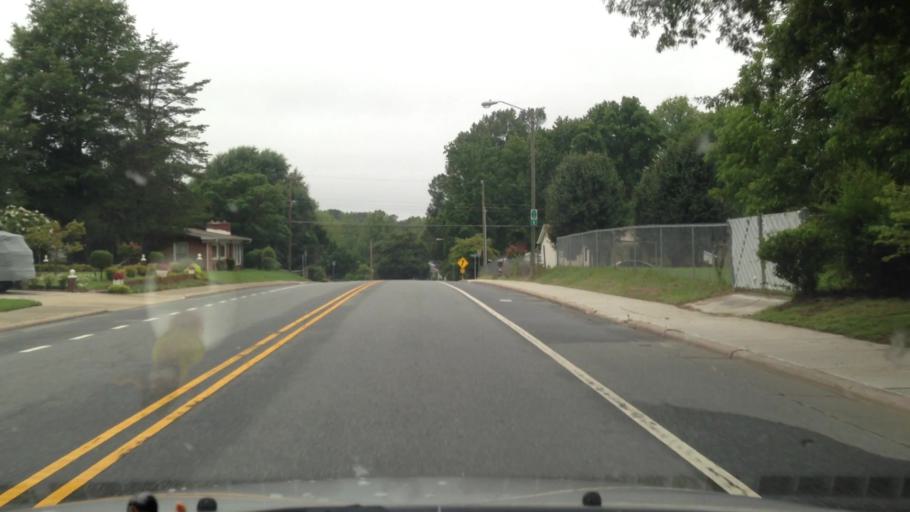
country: US
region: North Carolina
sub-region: Guilford County
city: Greensboro
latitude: 36.0541
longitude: -79.7647
